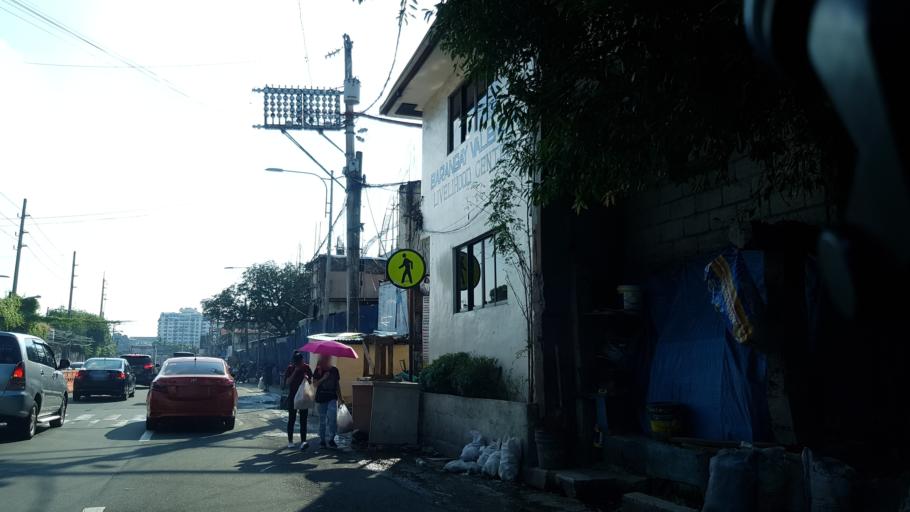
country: PH
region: Metro Manila
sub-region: San Juan
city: San Juan
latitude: 14.6088
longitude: 121.0409
